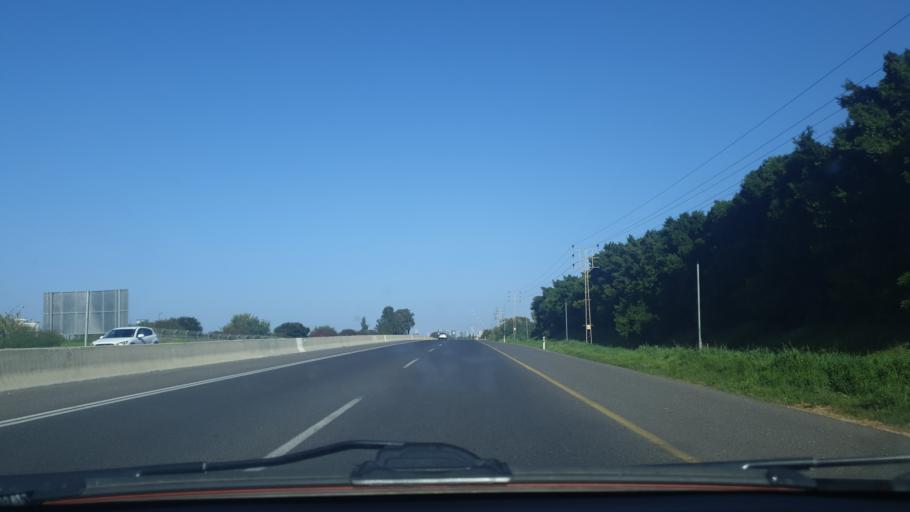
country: IL
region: Central District
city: Bet Dagan
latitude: 31.9941
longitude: 34.8262
